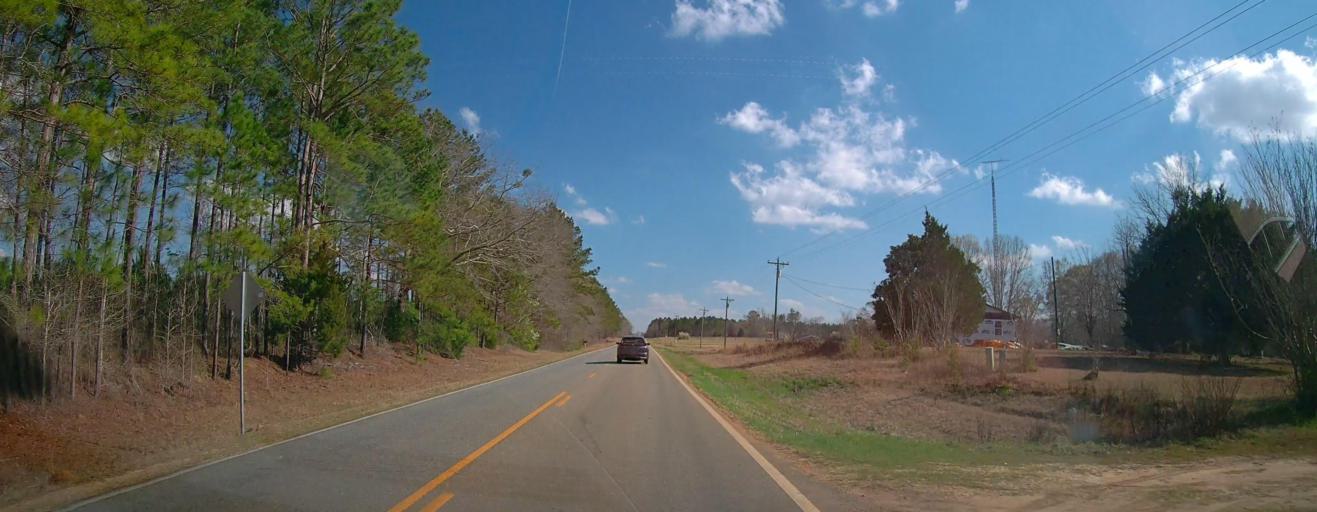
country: US
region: Georgia
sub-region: Laurens County
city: Dublin
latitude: 32.5827
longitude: -83.0541
